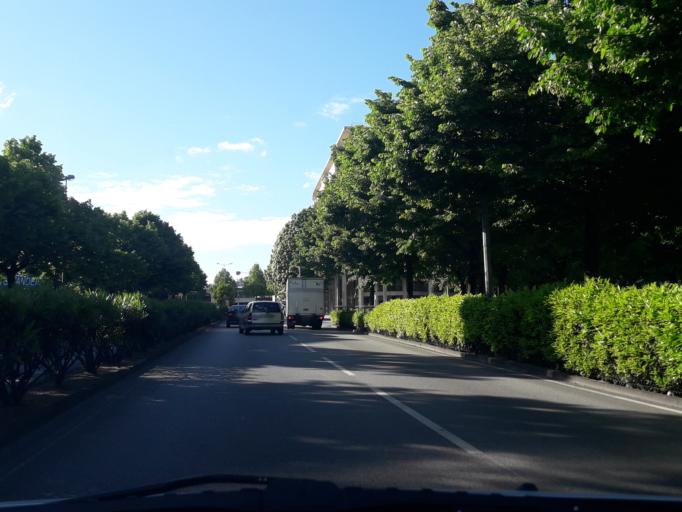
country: PT
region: Braga
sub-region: Vila Nova de Famalicao
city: Vila Nova de Famalicao
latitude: 41.4129
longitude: -8.5180
